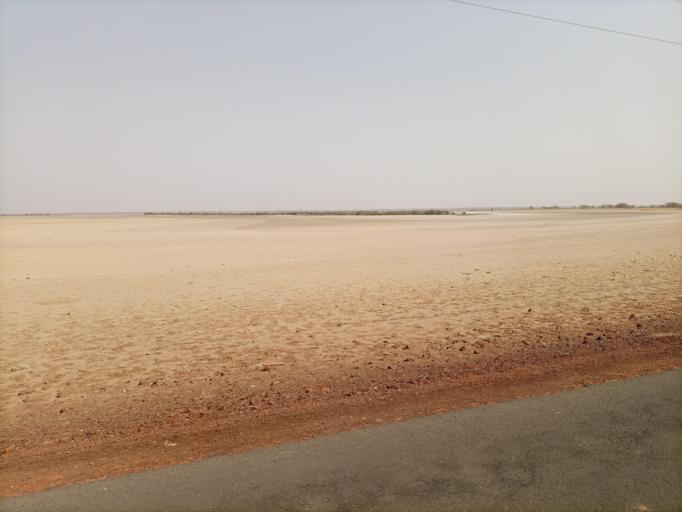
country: SN
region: Fatick
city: Foundiougne
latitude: 14.1664
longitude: -16.4635
